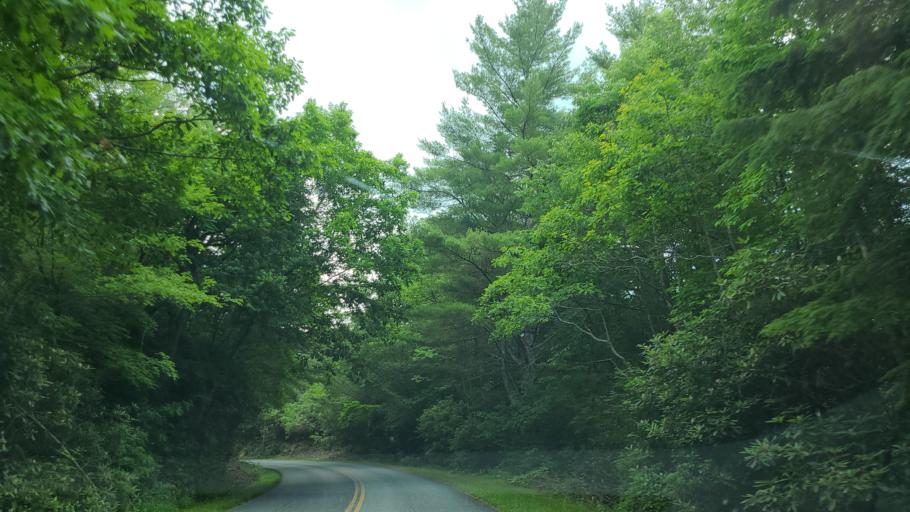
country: US
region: North Carolina
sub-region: Avery County
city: Newland
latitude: 35.9780
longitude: -81.9182
